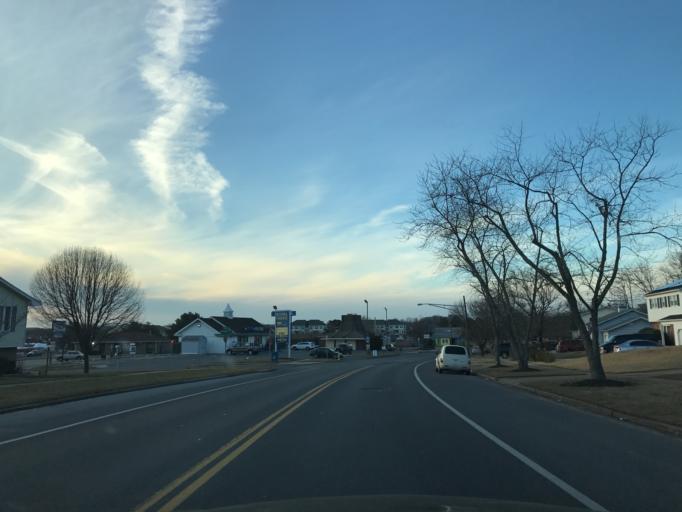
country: US
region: Maryland
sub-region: Harford County
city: Joppatowne
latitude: 39.4076
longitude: -76.3480
